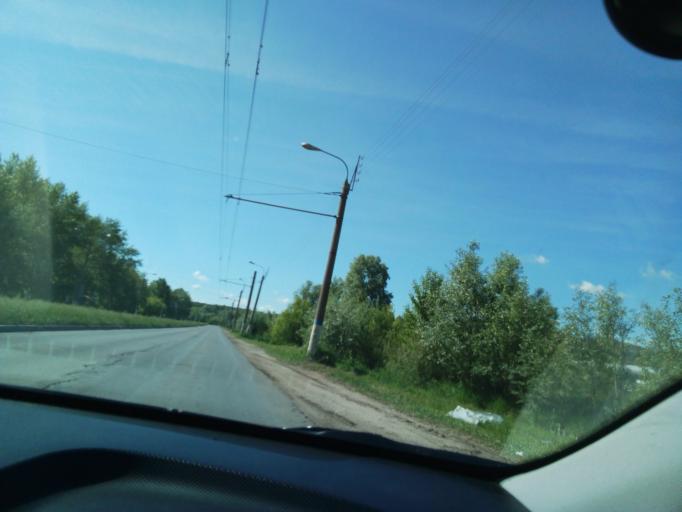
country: RU
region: Chuvashia
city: Novocheboksarsk
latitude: 56.0893
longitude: 47.5017
